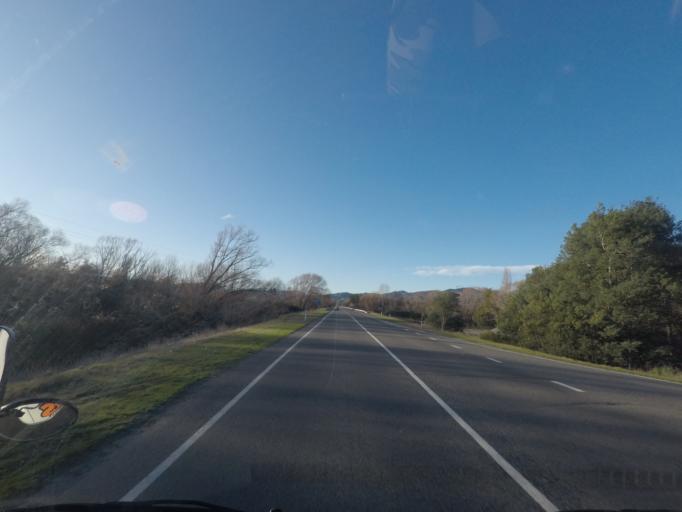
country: NZ
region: Canterbury
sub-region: Kaikoura District
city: Kaikoura
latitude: -42.7251
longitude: 173.2810
